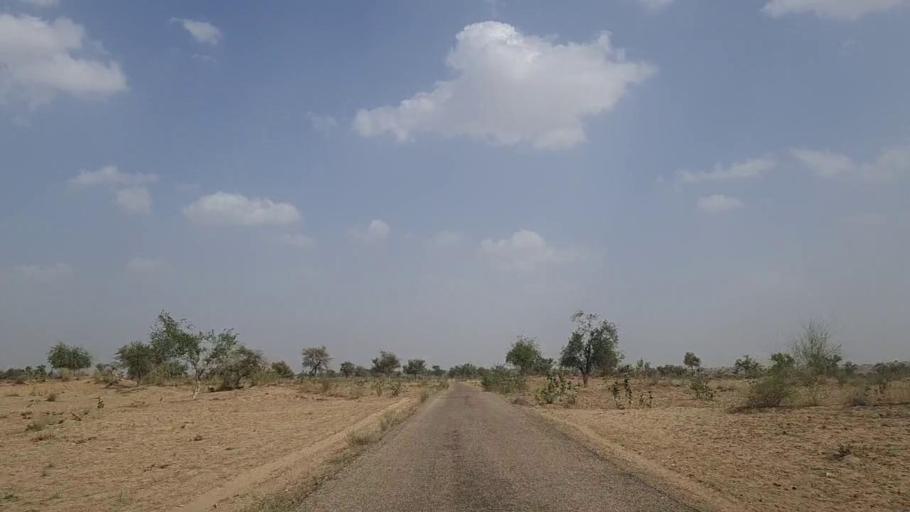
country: PK
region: Sindh
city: Islamkot
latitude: 24.8296
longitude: 70.1643
